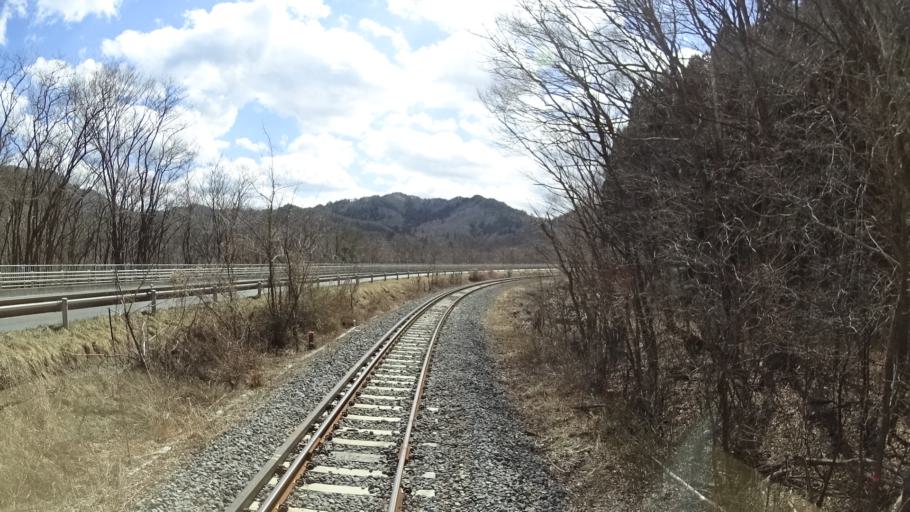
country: JP
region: Iwate
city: Yamada
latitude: 39.5480
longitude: 141.9391
